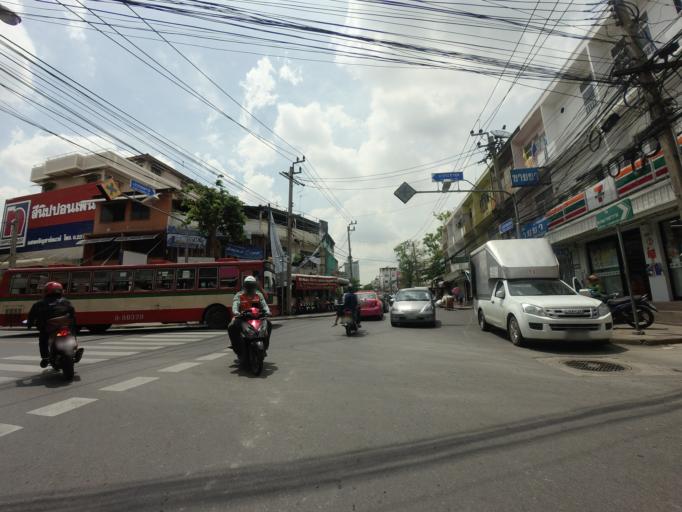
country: TH
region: Bangkok
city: Huai Khwang
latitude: 13.7785
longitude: 100.5668
